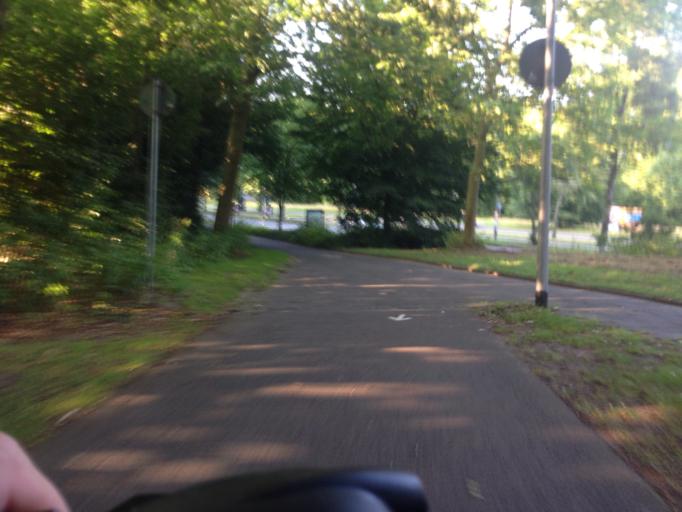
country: DE
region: North Rhine-Westphalia
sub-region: Regierungsbezirk Munster
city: Muenster
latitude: 51.9524
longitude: 7.6029
